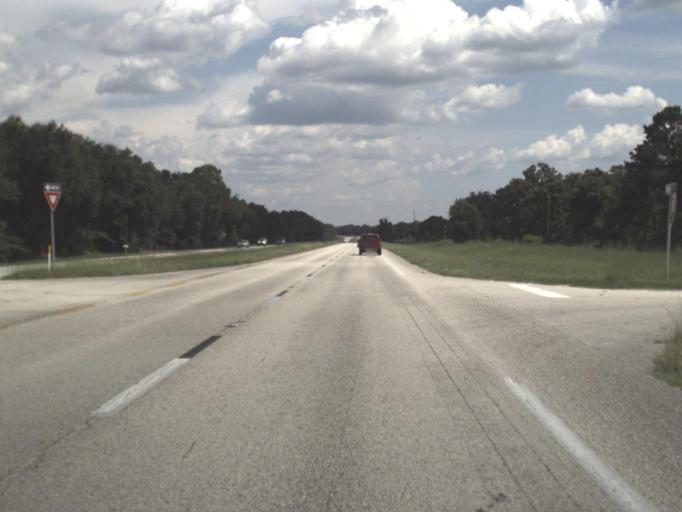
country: US
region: Florida
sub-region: Alachua County
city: Hawthorne
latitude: 29.6289
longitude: -82.1011
